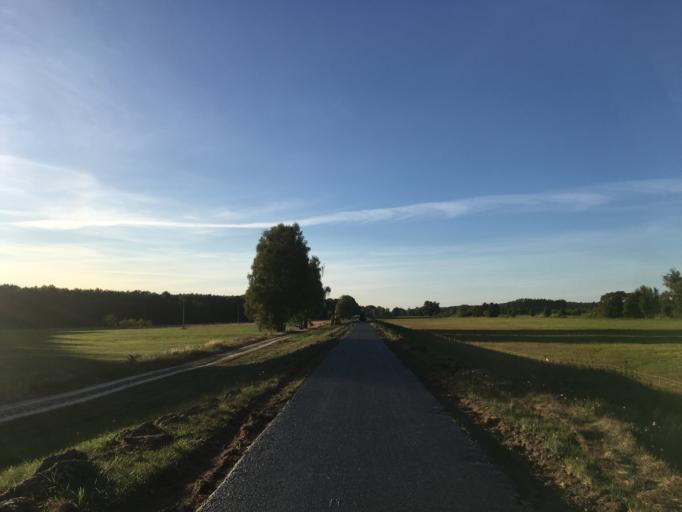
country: DE
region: Brandenburg
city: Forst
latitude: 51.6960
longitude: 14.7143
